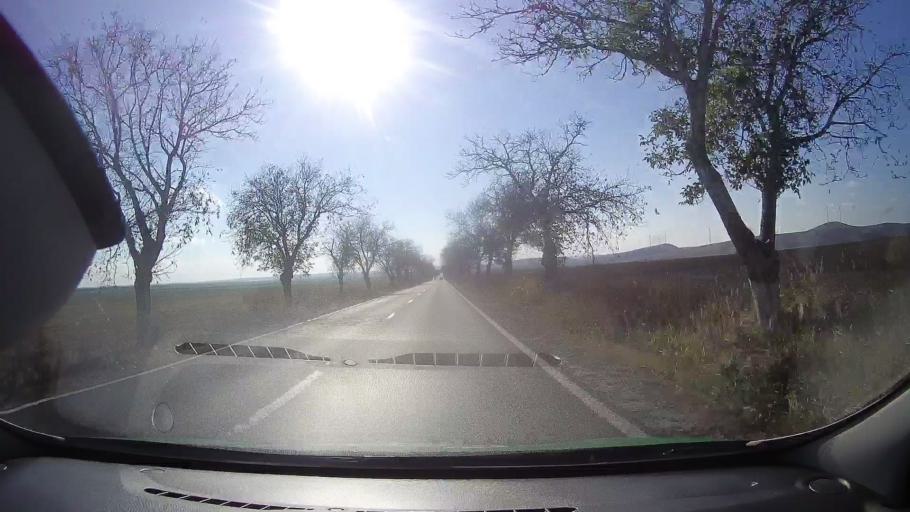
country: RO
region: Tulcea
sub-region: Comuna Ceamurlia de Jos
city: Ceamurlia de Jos
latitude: 44.8006
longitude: 28.6905
